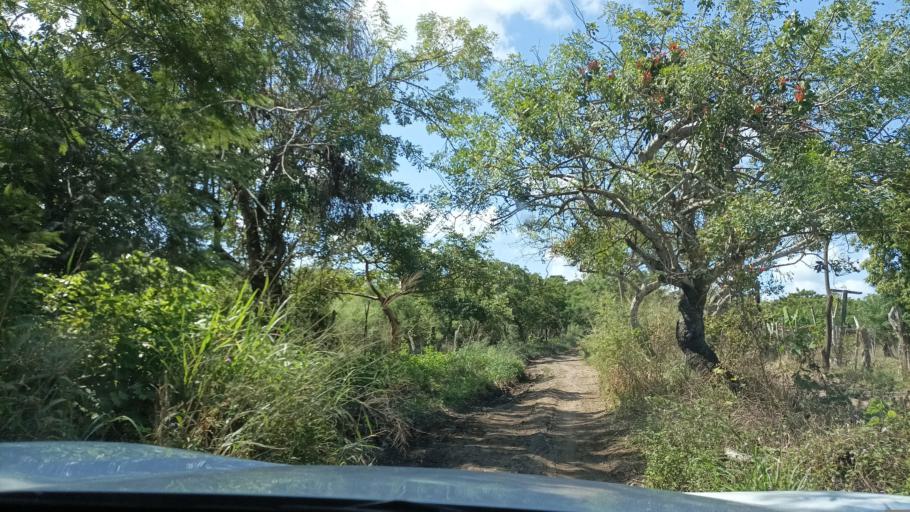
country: MX
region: Veracruz
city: Manlio Fabio Altamirano
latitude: 19.0886
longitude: -96.3403
